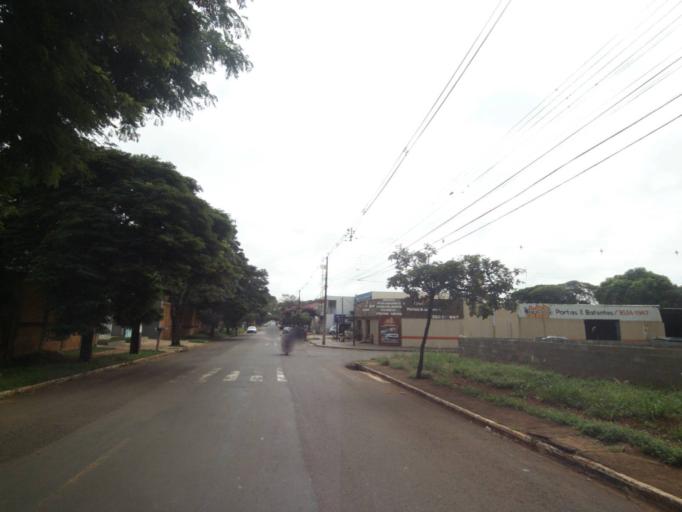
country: BR
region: Parana
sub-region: Campo Mourao
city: Campo Mourao
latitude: -24.0307
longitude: -52.3651
